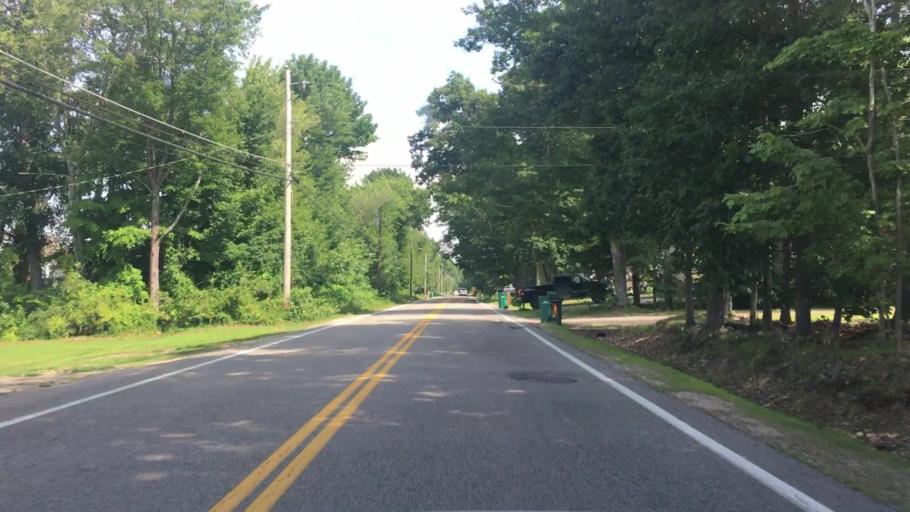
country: US
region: New Hampshire
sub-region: Strafford County
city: Rochester
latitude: 43.3164
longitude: -70.9378
